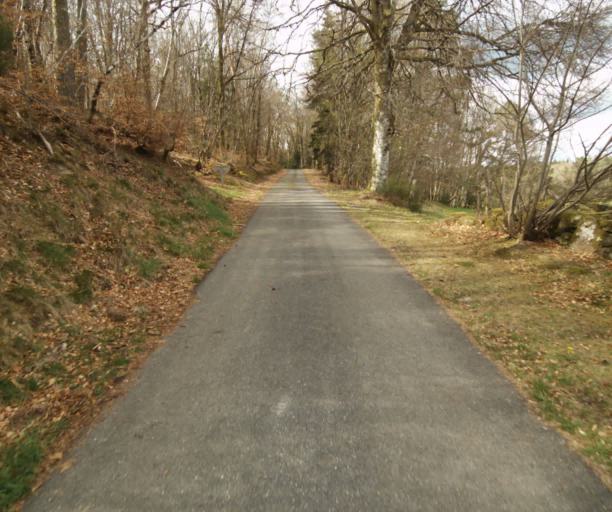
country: FR
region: Limousin
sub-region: Departement de la Correze
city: Argentat
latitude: 45.2123
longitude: 1.9657
